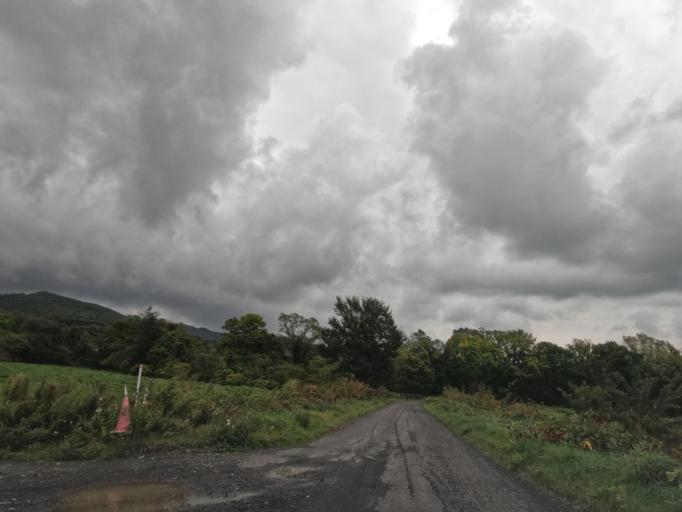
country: JP
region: Hokkaido
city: Date
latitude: 42.4938
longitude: 140.9023
